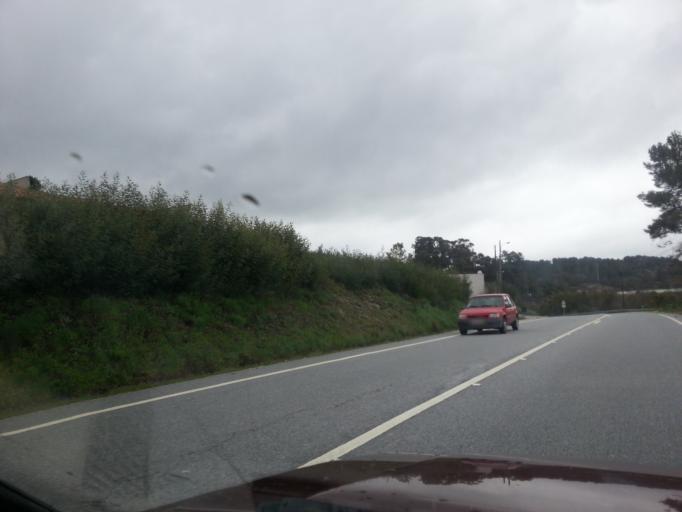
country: PT
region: Guarda
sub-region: Fornos de Algodres
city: Fornos de Algodres
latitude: 40.6160
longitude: -7.5202
